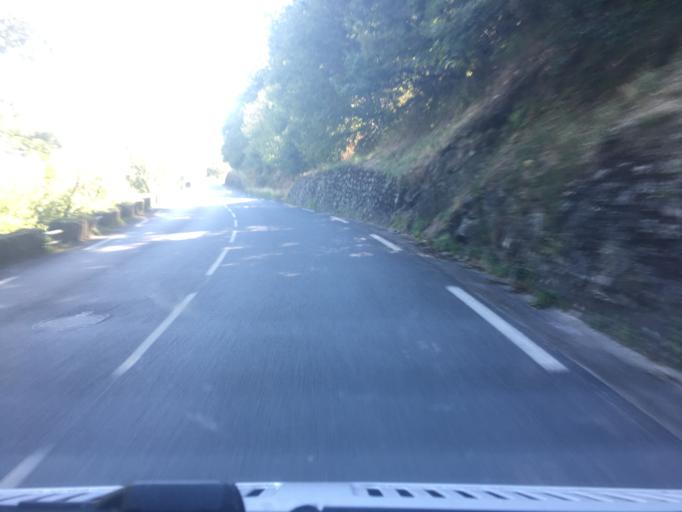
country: FR
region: Limousin
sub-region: Departement de la Correze
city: Bort-les-Orgues
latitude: 45.4090
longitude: 2.4988
